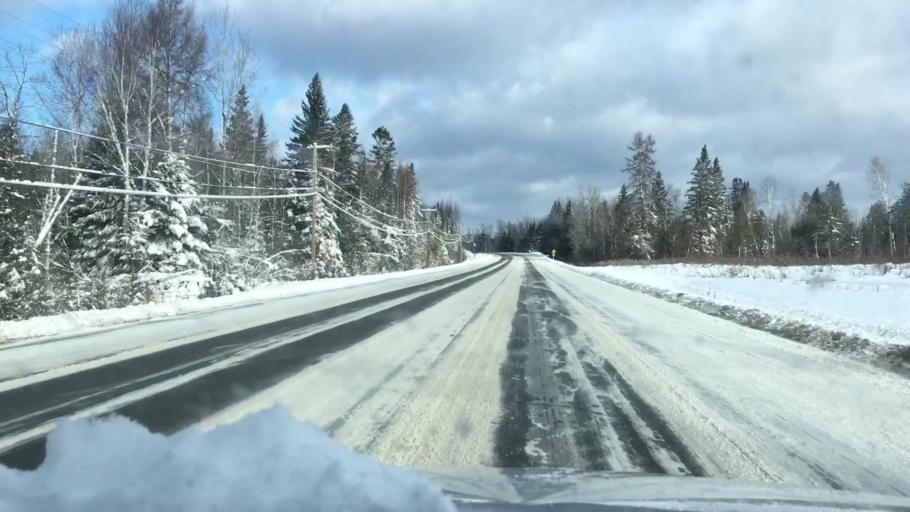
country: US
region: Maine
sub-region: Aroostook County
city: Caribou
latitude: 46.9223
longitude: -68.0197
